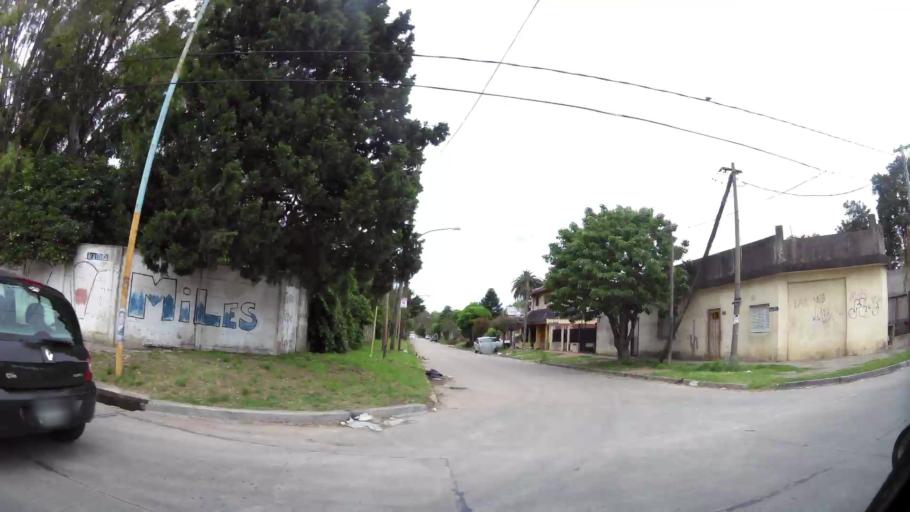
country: AR
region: Buenos Aires
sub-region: Partido de Quilmes
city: Quilmes
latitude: -34.7664
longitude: -58.2679
